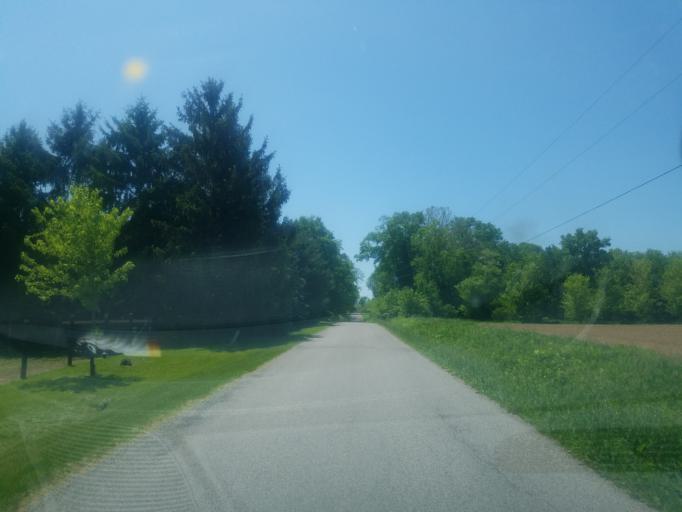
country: US
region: Ohio
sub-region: Huron County
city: Wakeman
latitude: 41.1935
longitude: -82.3702
